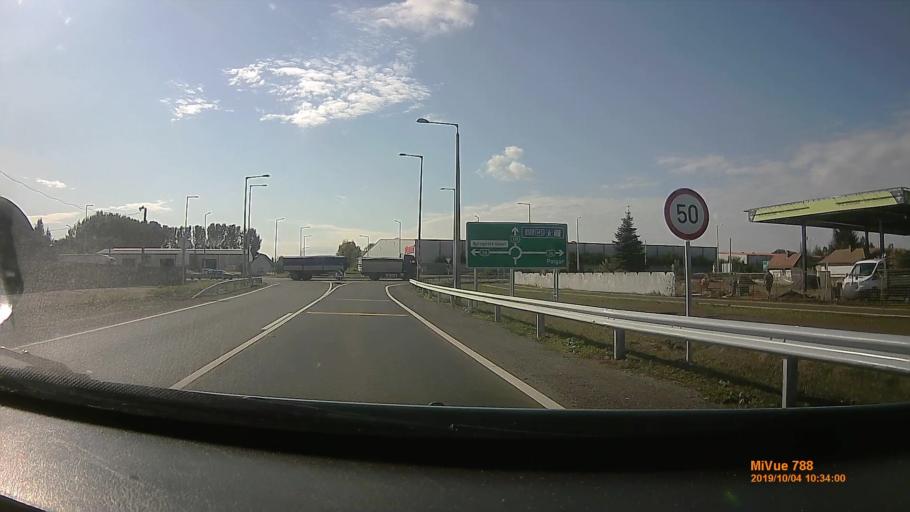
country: HU
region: Szabolcs-Szatmar-Bereg
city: Nyiregyhaza
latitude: 47.9579
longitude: 21.6559
